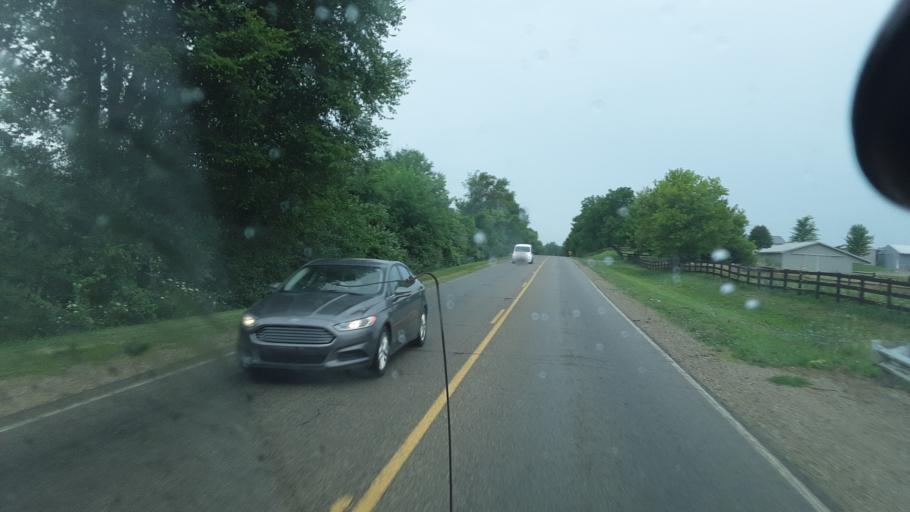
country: US
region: Indiana
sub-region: Steuben County
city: Fremont
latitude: 41.7076
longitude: -84.7983
